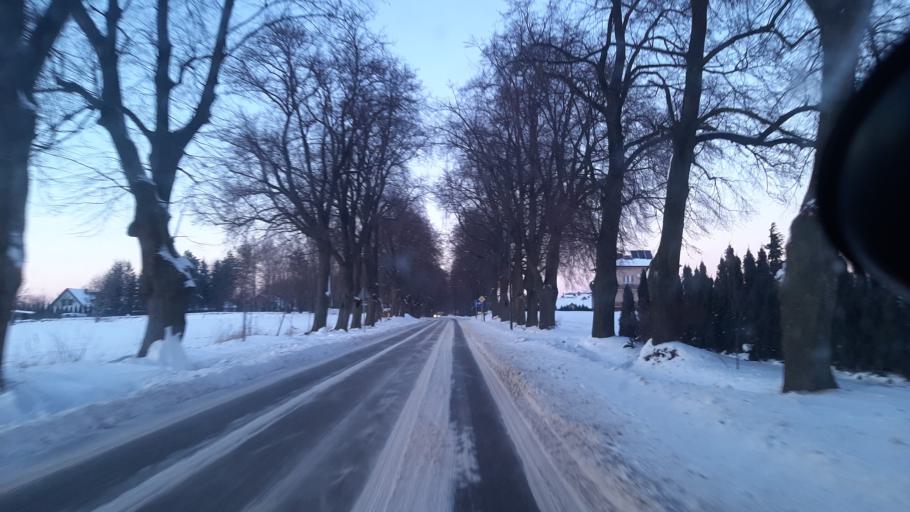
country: PL
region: Lublin Voivodeship
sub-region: Powiat lubelski
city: Lublin
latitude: 51.3234
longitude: 22.5608
